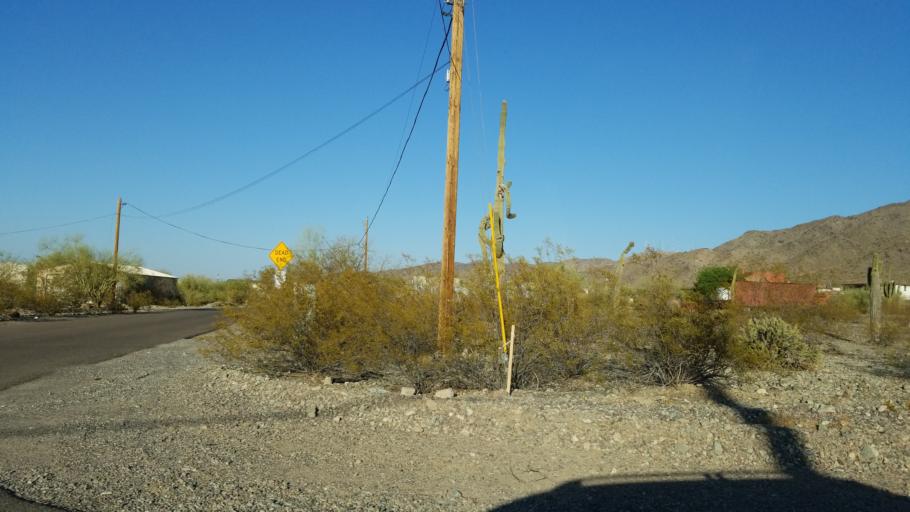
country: US
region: Arizona
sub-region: Maricopa County
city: Laveen
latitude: 33.3538
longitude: -112.1176
